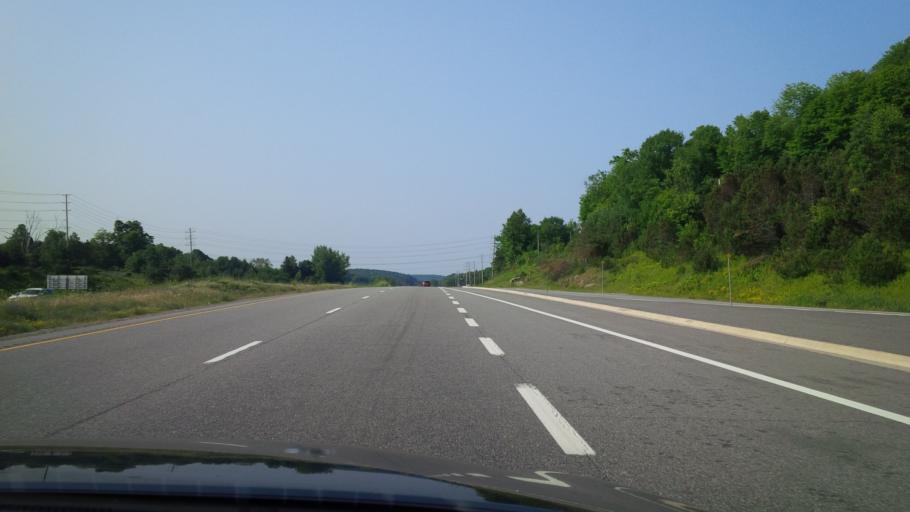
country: CA
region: Ontario
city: Huntsville
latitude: 45.3302
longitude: -79.2381
